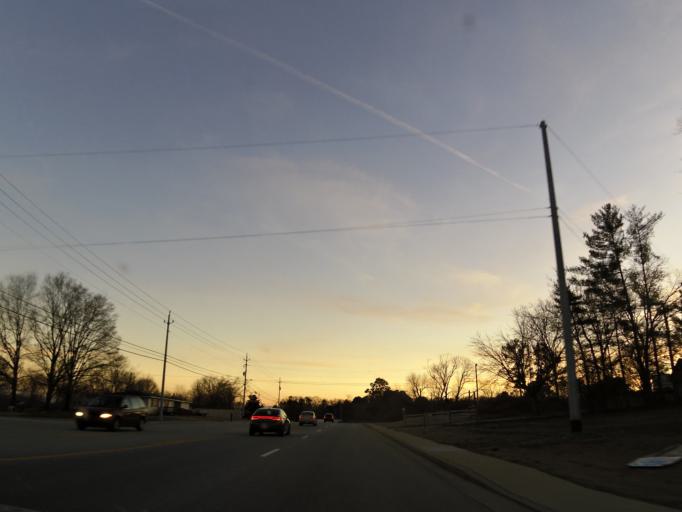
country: US
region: Tennessee
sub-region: Bradley County
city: Wildwood Lake
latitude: 35.1165
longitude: -84.8630
